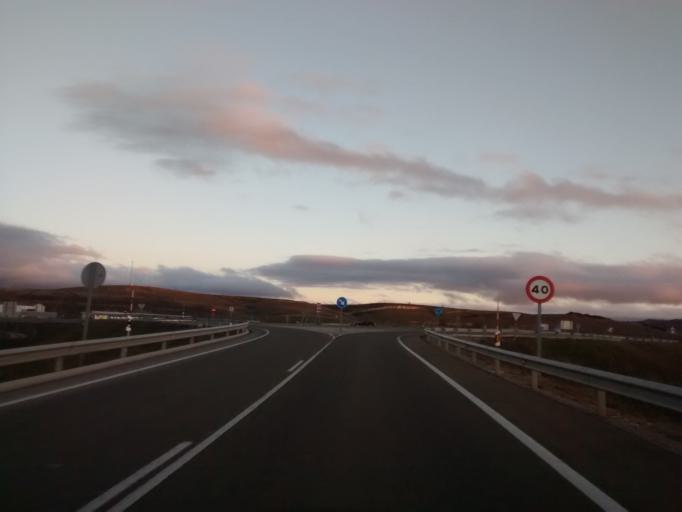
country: ES
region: Castille and Leon
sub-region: Provincia de Palencia
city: Aguilar de Campoo
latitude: 42.7818
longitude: -4.2435
